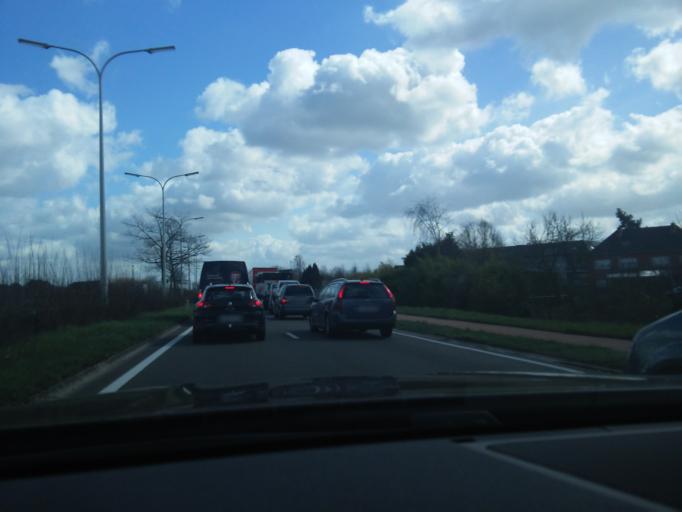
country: BE
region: Flanders
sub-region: Provincie Antwerpen
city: Bornem
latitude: 51.1018
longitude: 4.2452
